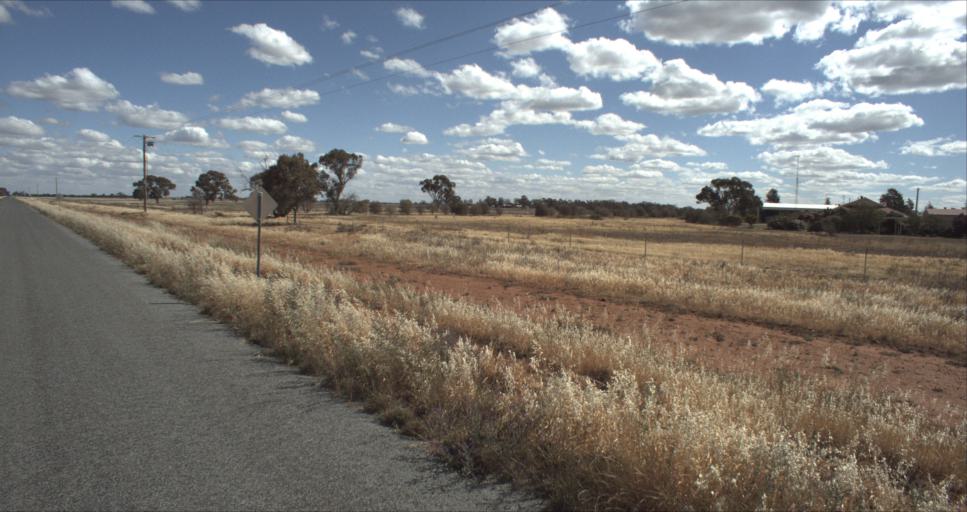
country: AU
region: New South Wales
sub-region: Leeton
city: Leeton
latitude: -34.4602
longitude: 146.2529
